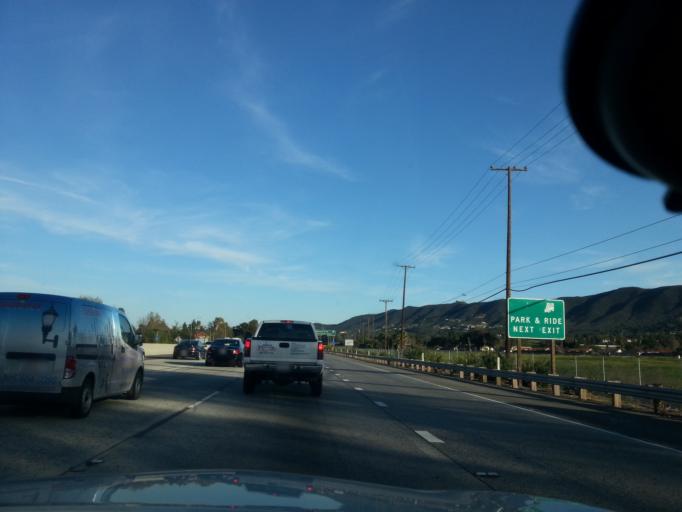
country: US
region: California
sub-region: Ventura County
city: Casa Conejo
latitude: 34.1870
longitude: -118.9331
